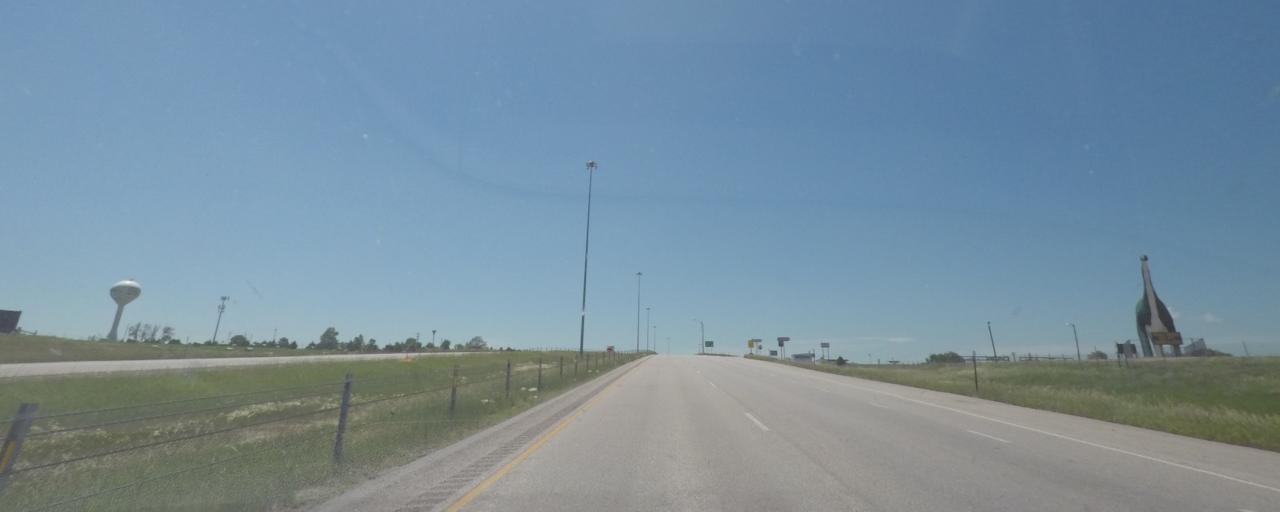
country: US
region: South Dakota
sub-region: Haakon County
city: Philip
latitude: 43.9877
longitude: -102.2325
